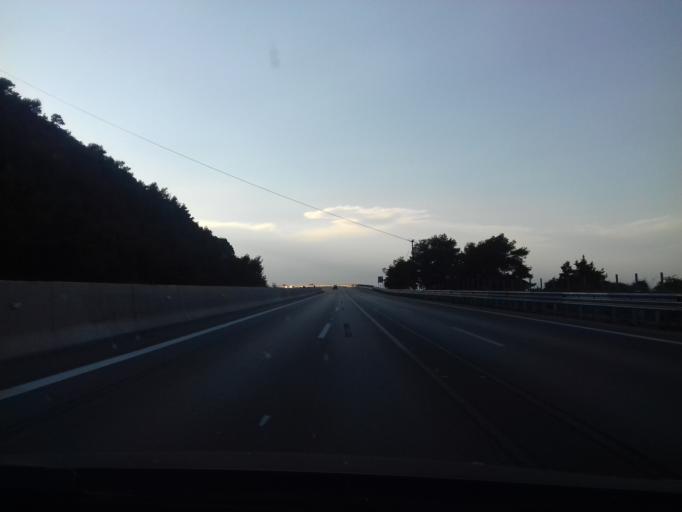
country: GR
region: West Greece
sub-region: Nomos Achaias
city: Siliveniotika
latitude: 38.1687
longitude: 22.3262
